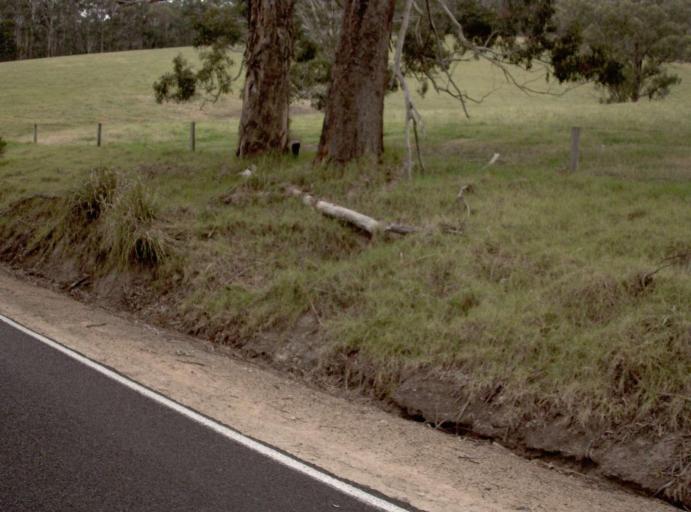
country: AU
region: New South Wales
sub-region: Bombala
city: Bombala
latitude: -37.4815
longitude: 149.1807
